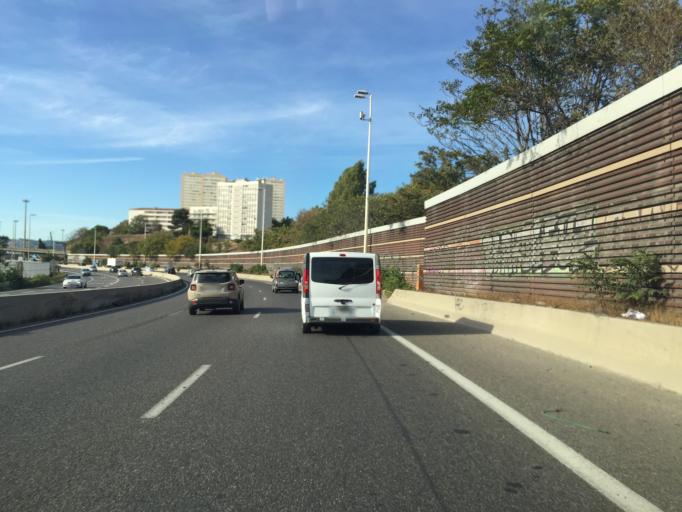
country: FR
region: Provence-Alpes-Cote d'Azur
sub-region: Departement des Bouches-du-Rhone
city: Marseille 14
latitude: 43.3344
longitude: 5.3542
